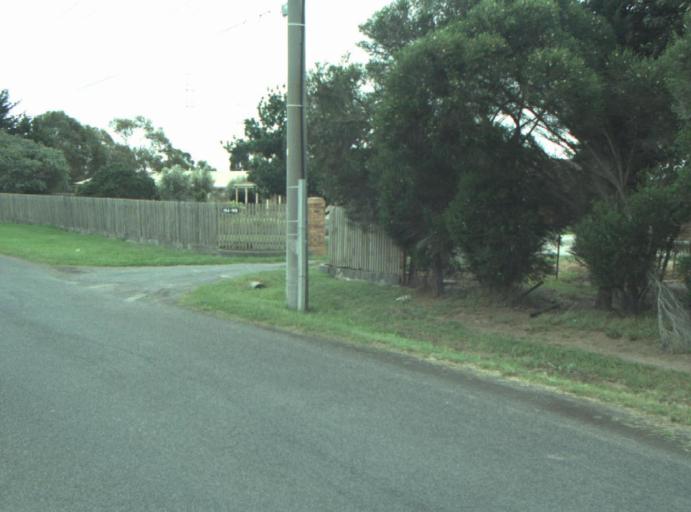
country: AU
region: Victoria
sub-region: Greater Geelong
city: Bell Post Hill
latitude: -38.0700
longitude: 144.3394
